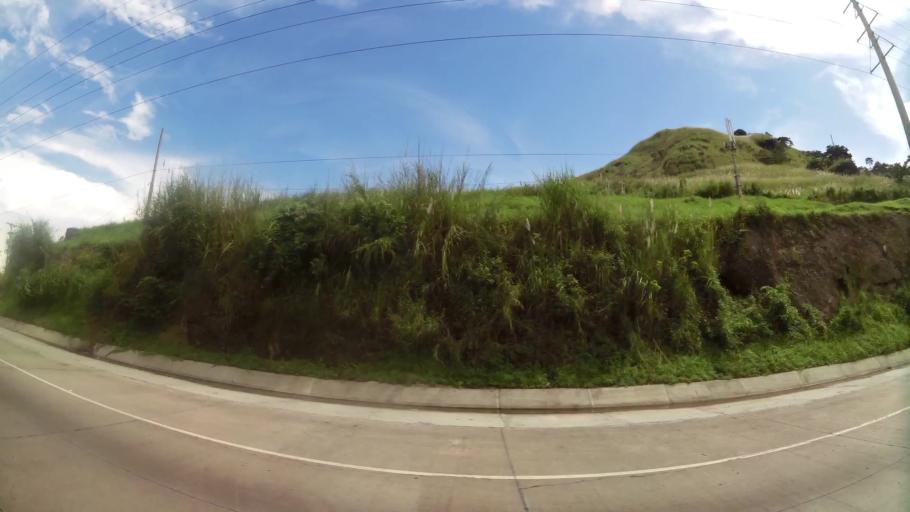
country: PA
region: Panama
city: Las Cumbres
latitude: 9.0540
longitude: -79.5181
